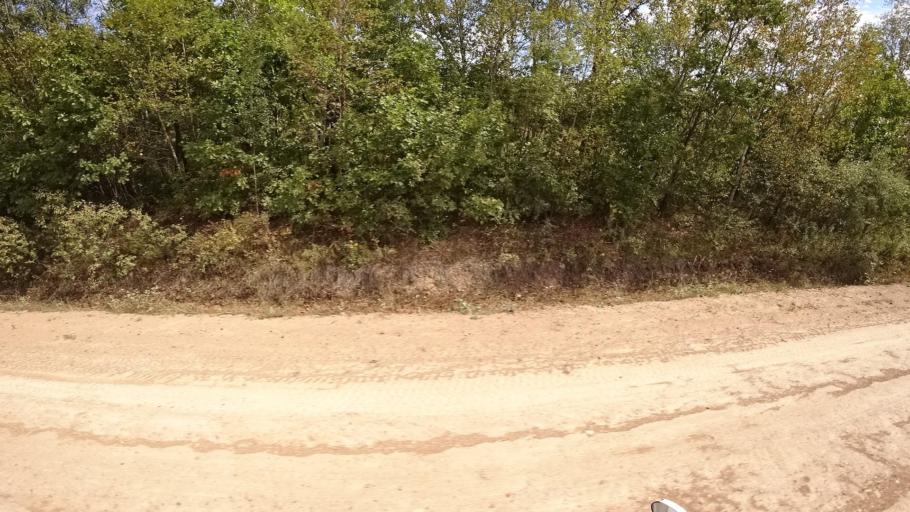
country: RU
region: Primorskiy
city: Yakovlevka
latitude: 44.7289
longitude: 133.6097
